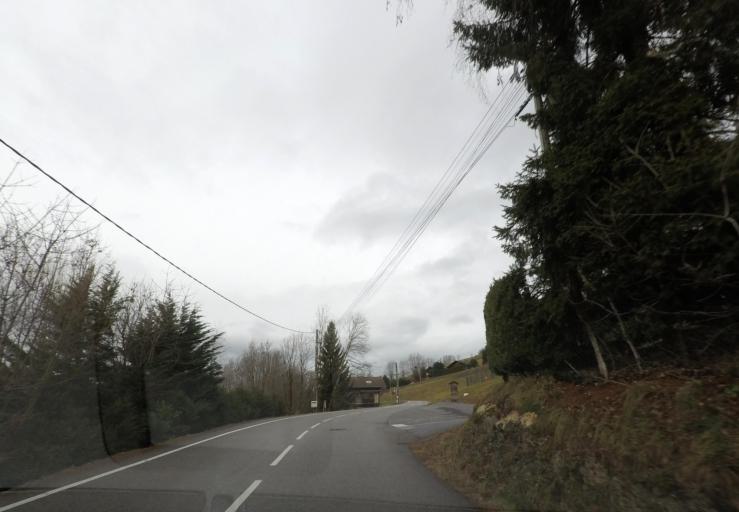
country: FR
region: Rhone-Alpes
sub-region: Departement de la Haute-Savoie
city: Chatillon-sur-Cluses
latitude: 46.0751
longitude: 6.6118
